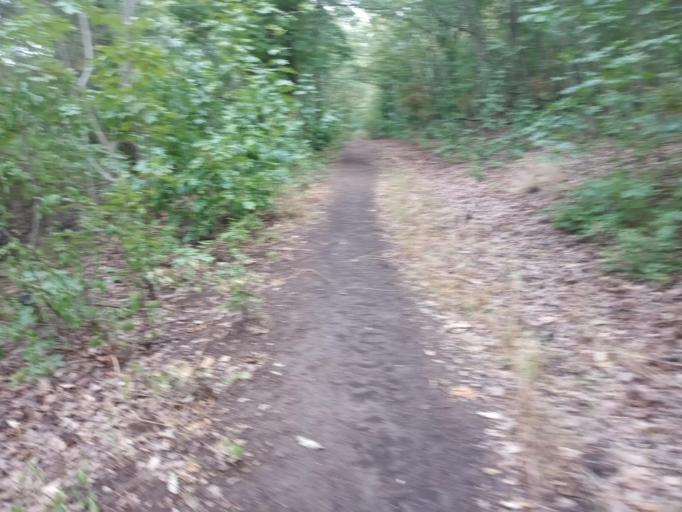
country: HU
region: Pest
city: Pilisborosjeno
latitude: 47.6249
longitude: 18.9991
